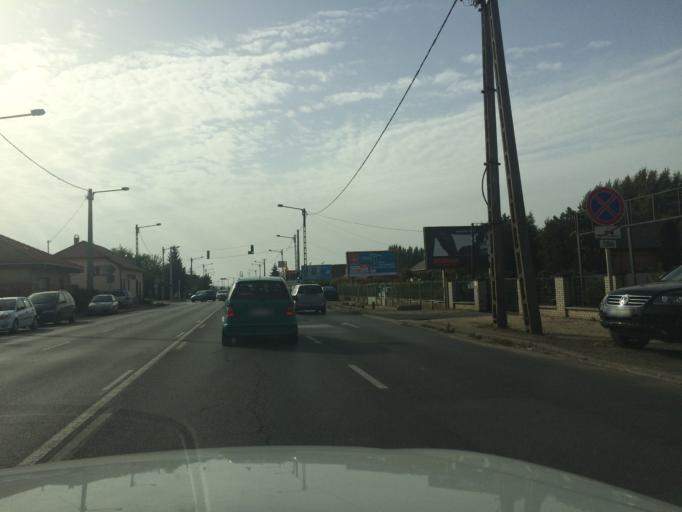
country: HU
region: Szabolcs-Szatmar-Bereg
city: Nyiregyhaza
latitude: 47.9265
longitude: 21.7186
